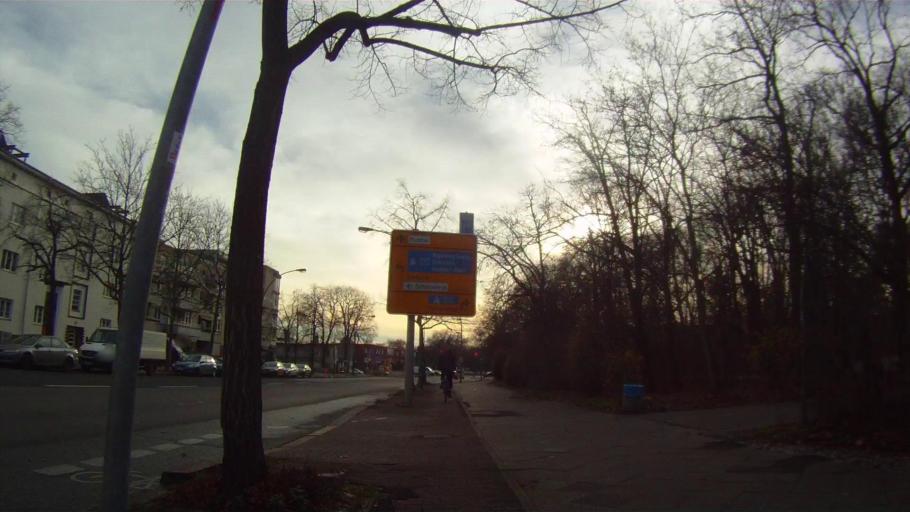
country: DE
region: Berlin
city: Britz
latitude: 52.4537
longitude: 13.4515
